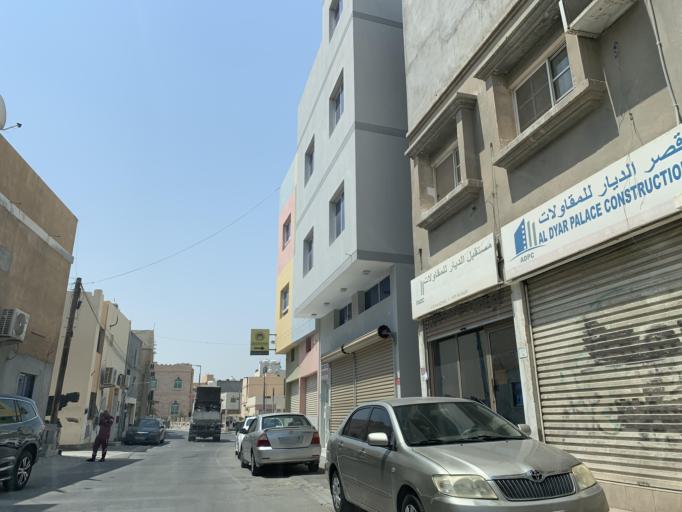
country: BH
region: Manama
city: Jidd Hafs
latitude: 26.2043
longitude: 50.5202
